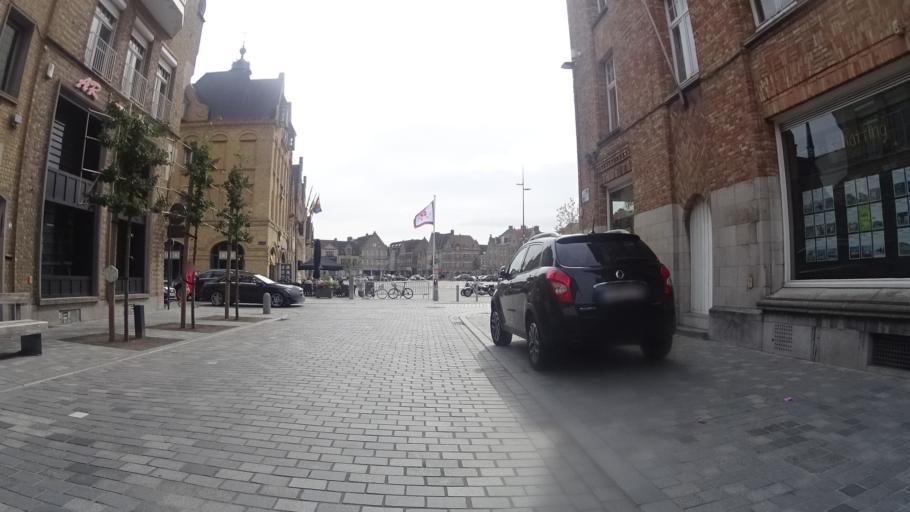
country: BE
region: Flanders
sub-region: Provincie West-Vlaanderen
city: Diksmuide
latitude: 51.0335
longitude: 2.8635
